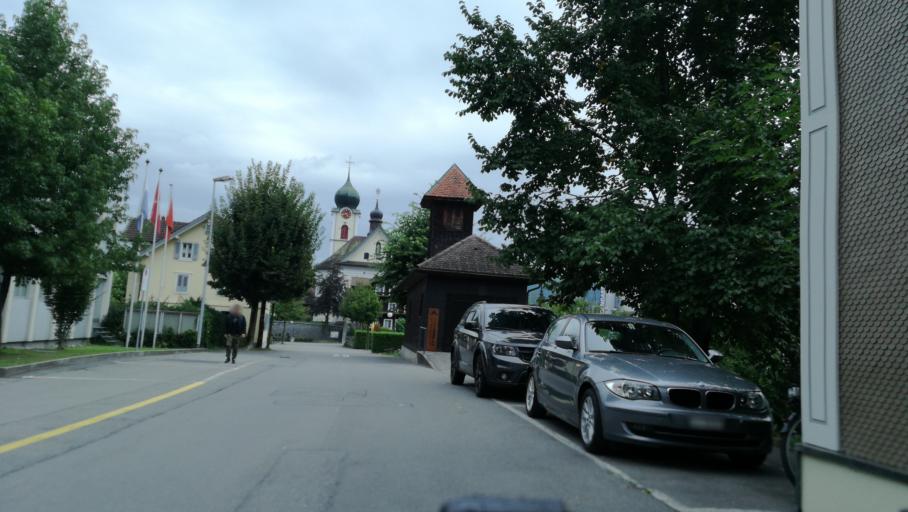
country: CH
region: Lucerne
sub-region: Lucerne-Land District
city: Ebikon
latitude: 47.0807
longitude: 8.3387
